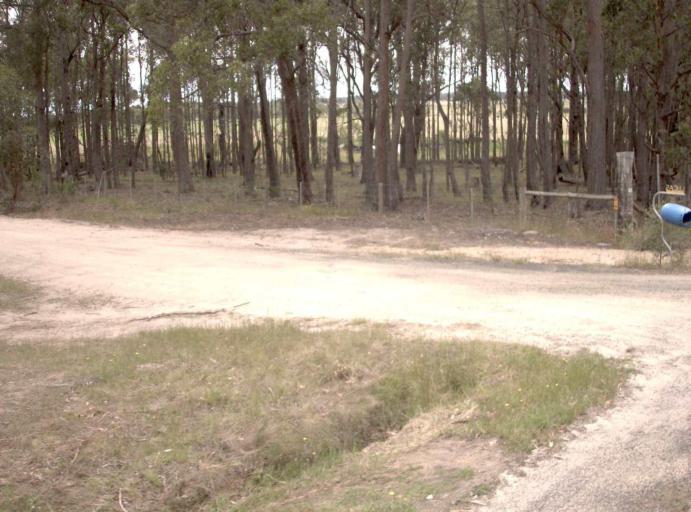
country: AU
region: Victoria
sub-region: Latrobe
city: Traralgon
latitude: -38.4767
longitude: 146.8218
